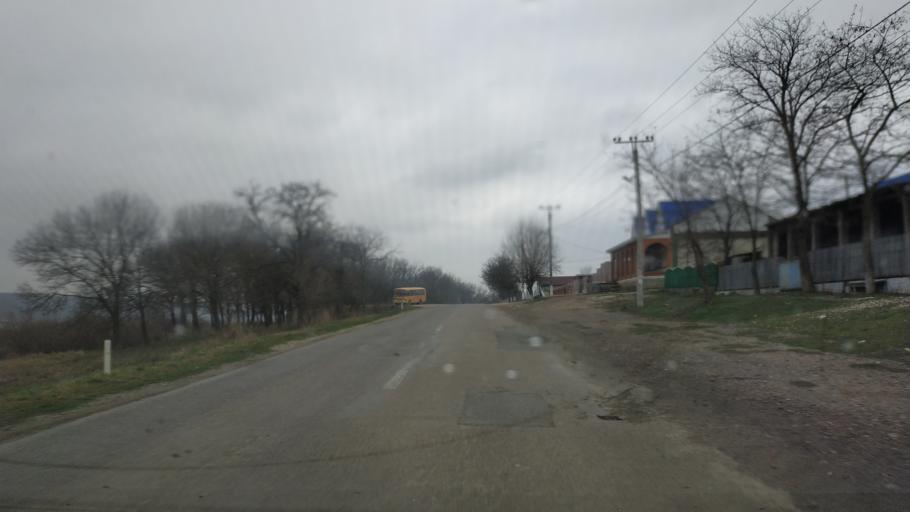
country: MD
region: Cantemir
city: Cantemir
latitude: 46.3430
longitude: 28.3058
